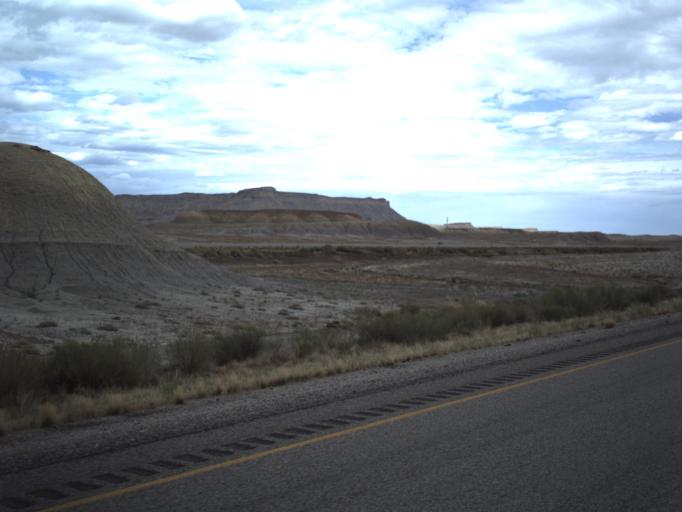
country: US
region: Utah
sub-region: Grand County
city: Moab
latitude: 38.9336
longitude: -110.0215
